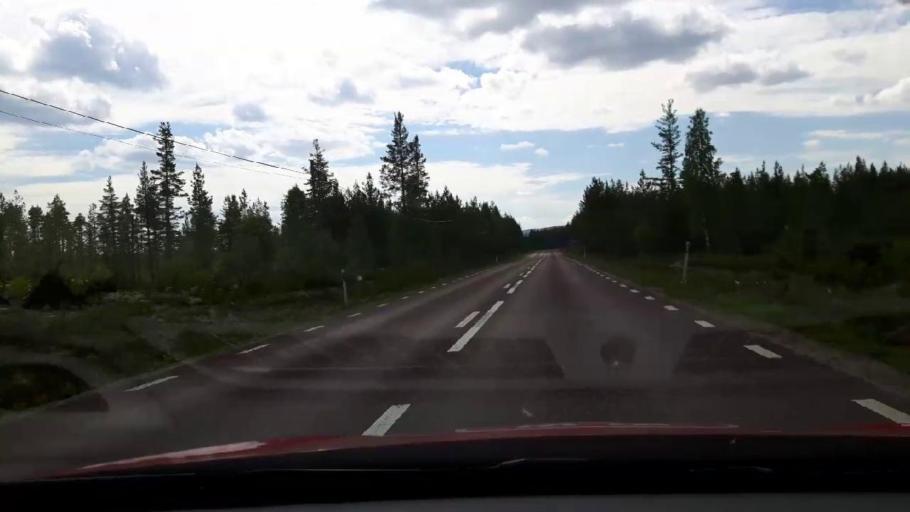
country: SE
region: Jaemtland
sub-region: Harjedalens Kommun
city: Sveg
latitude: 62.1230
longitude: 14.9708
